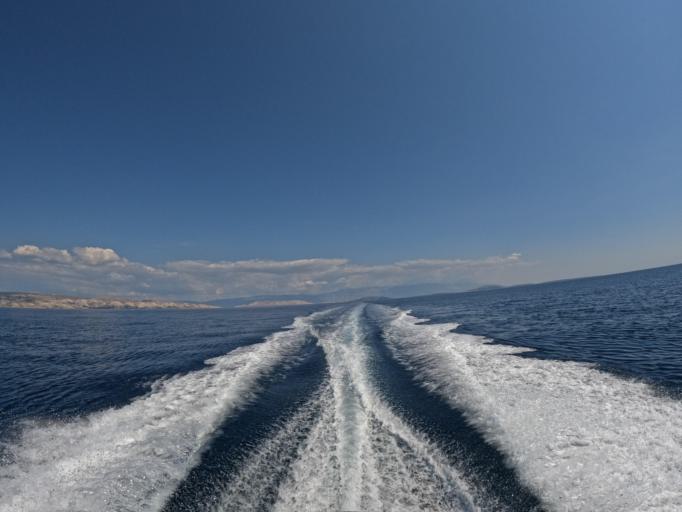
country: HR
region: Primorsko-Goranska
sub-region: Grad Krk
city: Krk
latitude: 44.9208
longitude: 14.5623
